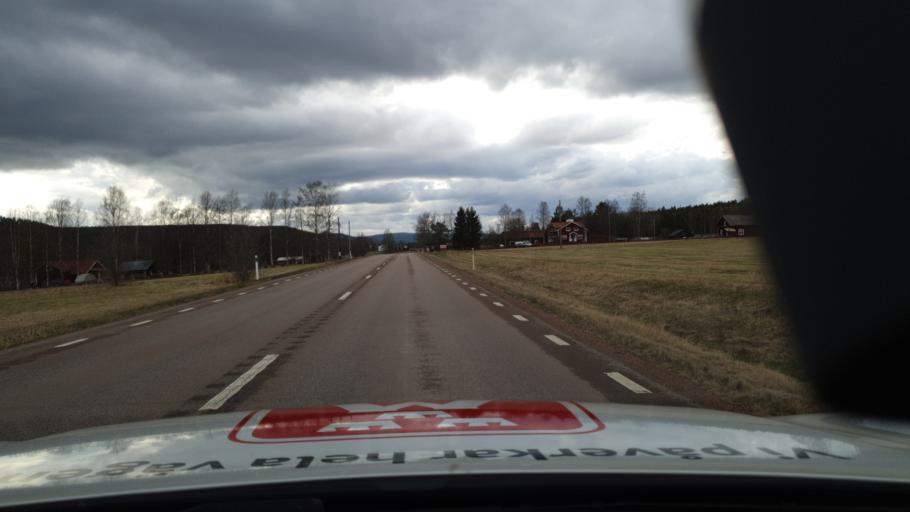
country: SE
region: Jaemtland
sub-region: Braecke Kommun
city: Braecke
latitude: 63.1663
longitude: 15.6731
